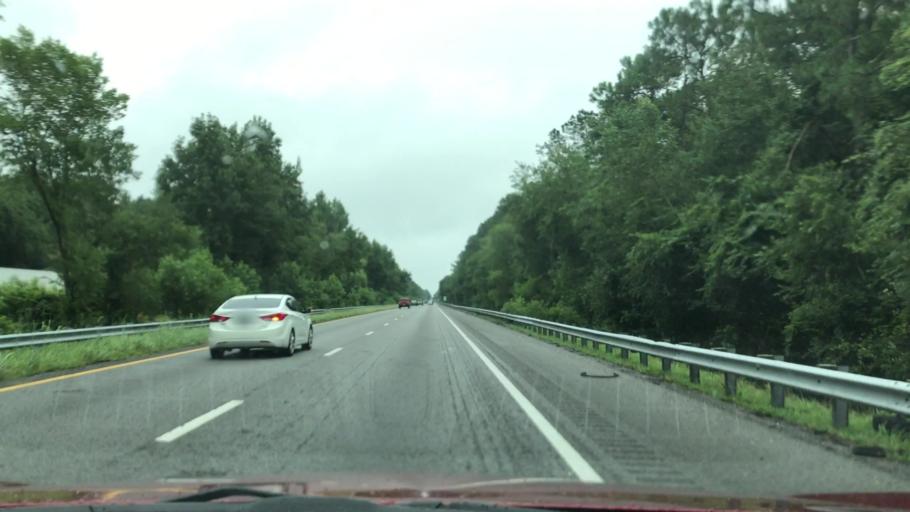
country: US
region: South Carolina
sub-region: Dorchester County
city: Ridgeville
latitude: 33.1513
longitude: -80.3403
